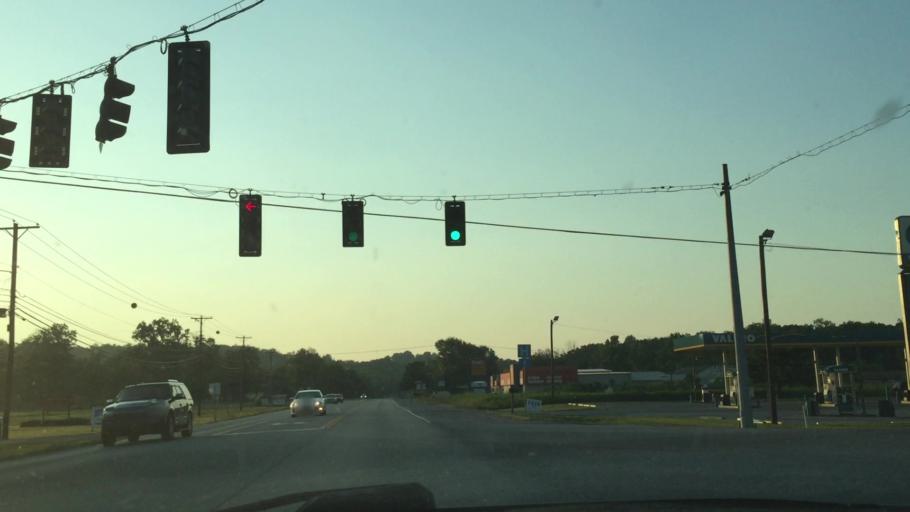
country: US
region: Kentucky
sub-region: Carroll County
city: Carrollton
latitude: 38.6639
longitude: -85.1413
